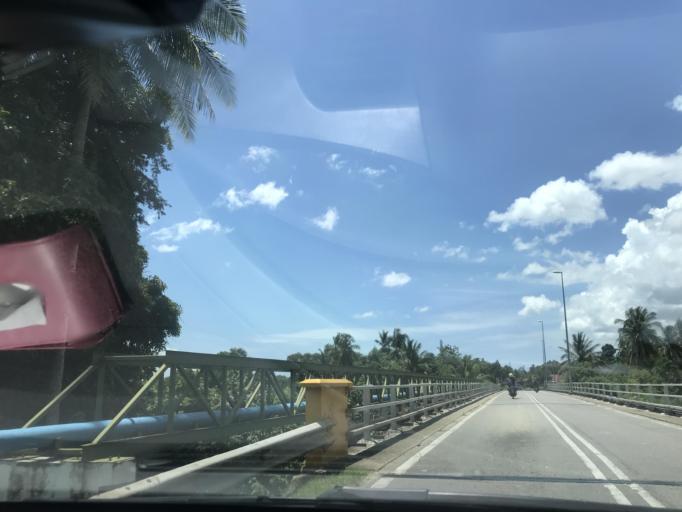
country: MY
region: Kelantan
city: Tumpat
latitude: 6.1931
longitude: 102.1461
